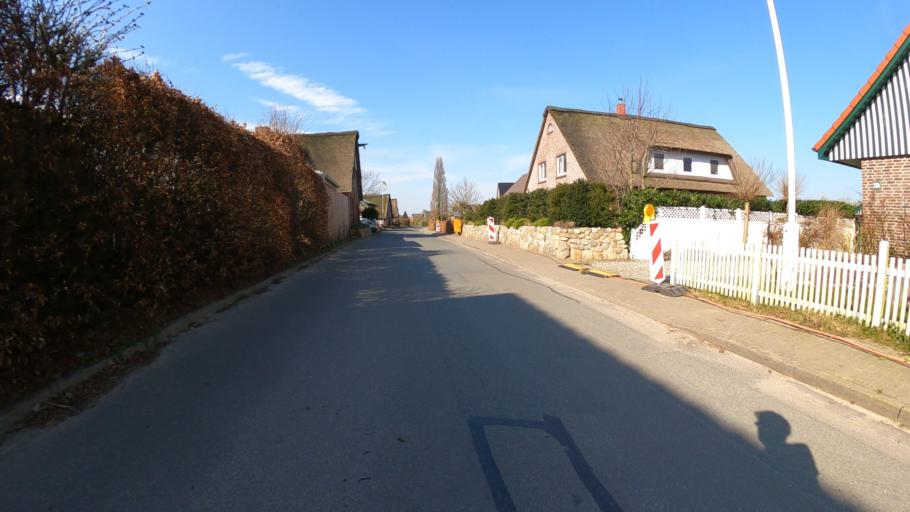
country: DE
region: Schleswig-Holstein
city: Seestermuhe
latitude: 53.7061
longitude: 9.5572
